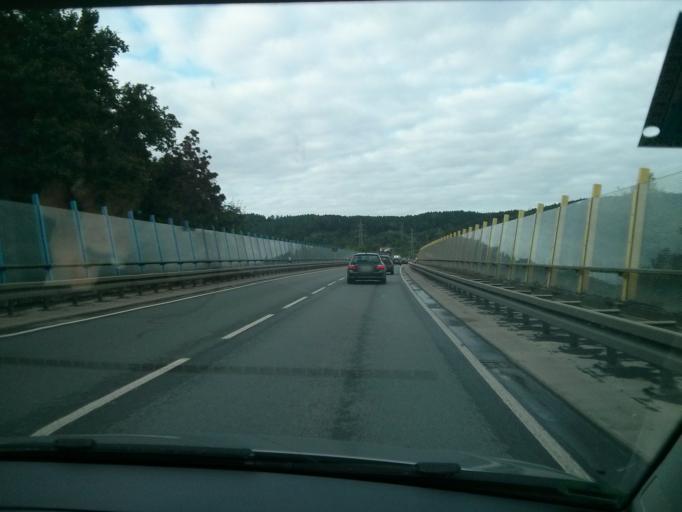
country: DE
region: North Rhine-Westphalia
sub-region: Regierungsbezirk Arnsberg
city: Sundern
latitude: 51.4306
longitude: 7.9888
